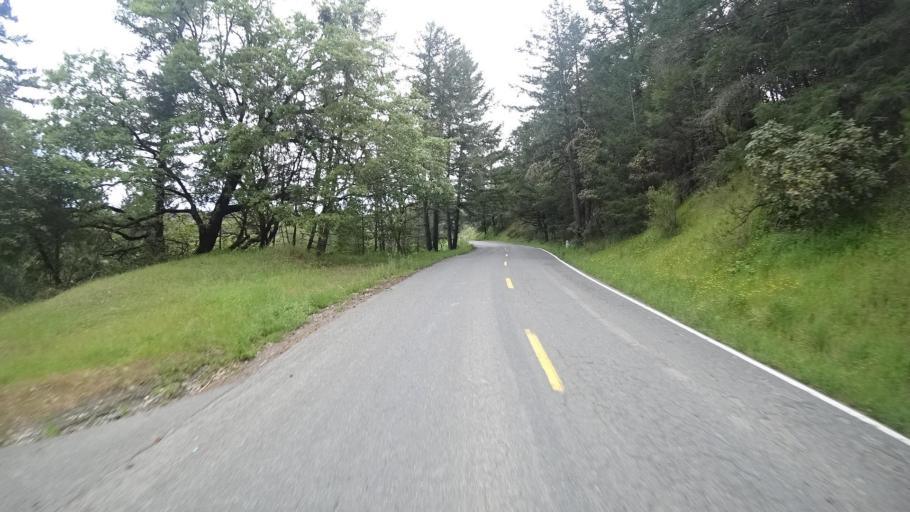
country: US
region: California
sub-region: Humboldt County
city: Redway
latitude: 40.1117
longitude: -123.7762
